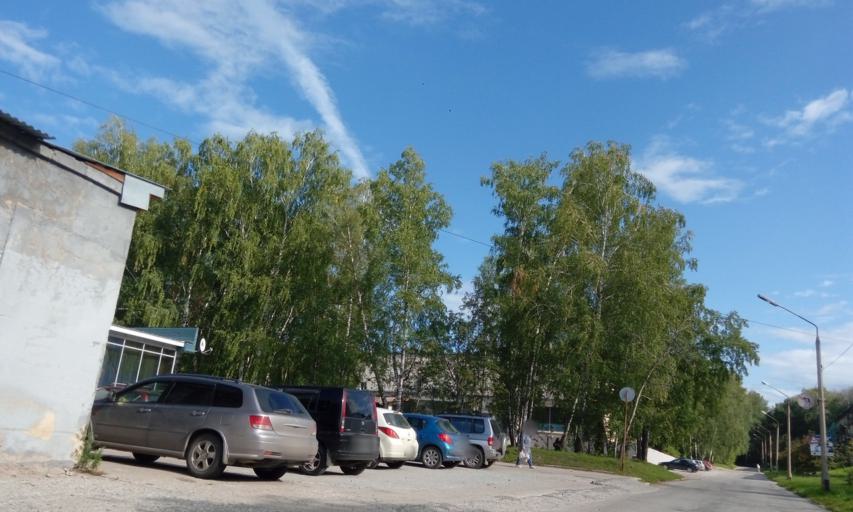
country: RU
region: Novosibirsk
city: Akademgorodok
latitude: 54.8390
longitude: 83.0951
